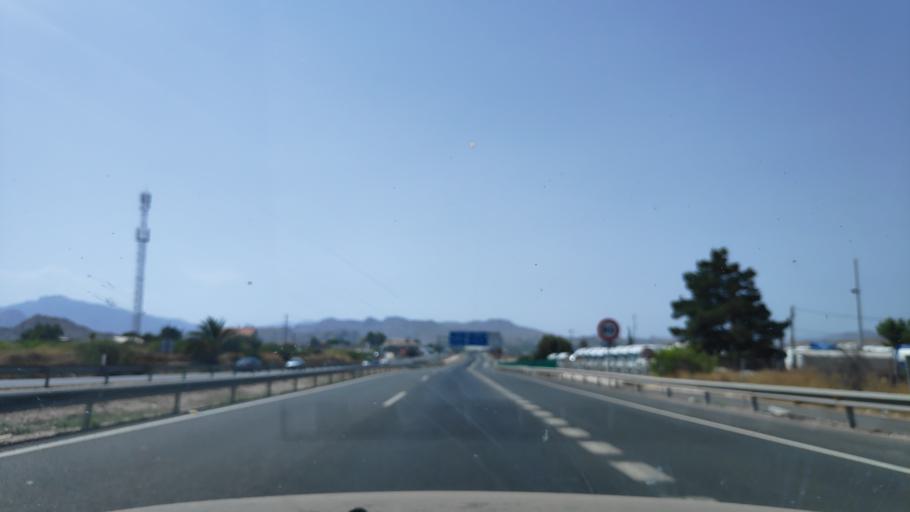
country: ES
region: Murcia
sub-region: Murcia
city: Lorqui
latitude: 38.1212
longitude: -1.2492
